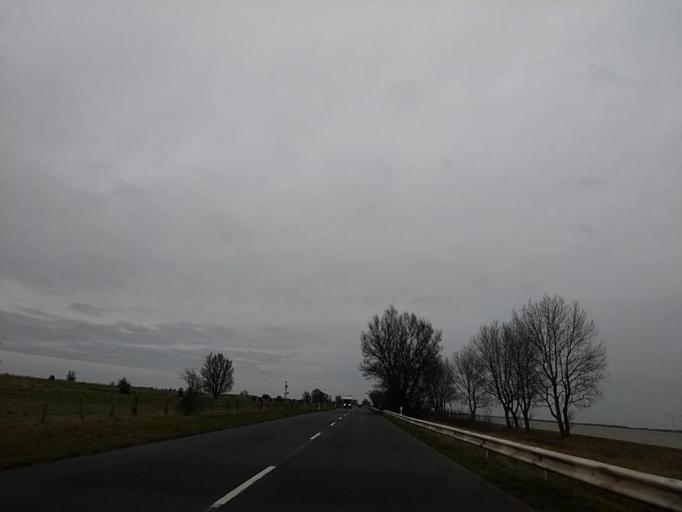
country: NL
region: Groningen
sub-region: Gemeente Delfzijl
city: Delfzijl
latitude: 53.3495
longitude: 7.0097
